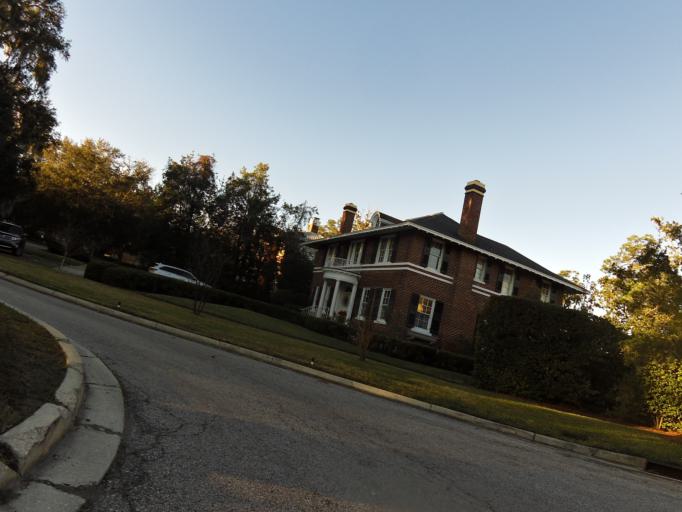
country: US
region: Florida
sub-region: Duval County
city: Jacksonville
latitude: 30.2989
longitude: -81.6990
